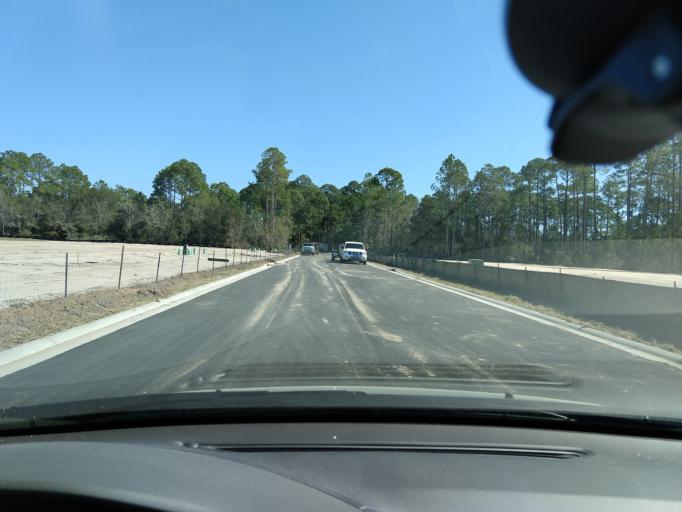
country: US
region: Florida
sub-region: Walton County
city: Miramar Beach
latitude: 30.3823
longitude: -86.2893
